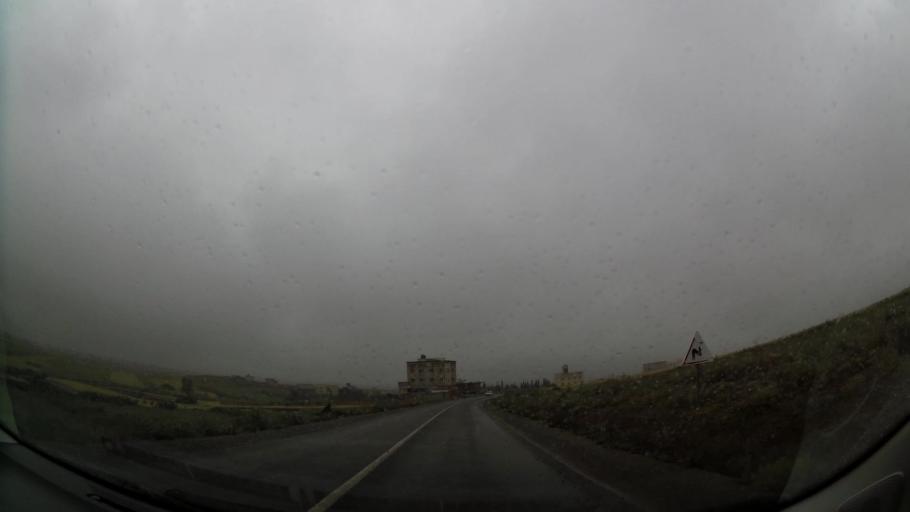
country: MA
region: Oriental
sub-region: Nador
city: Boudinar
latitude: 35.1403
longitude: -3.6119
